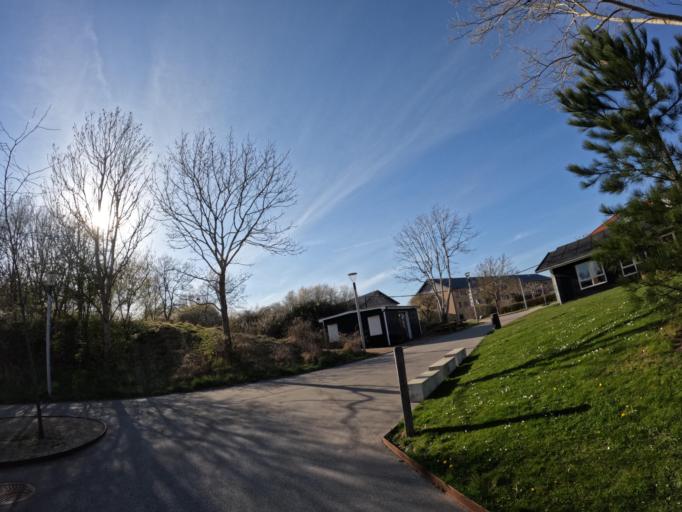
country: DK
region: Capital Region
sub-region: Hoje-Taastrup Kommune
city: Flong
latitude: 55.6480
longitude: 12.2154
